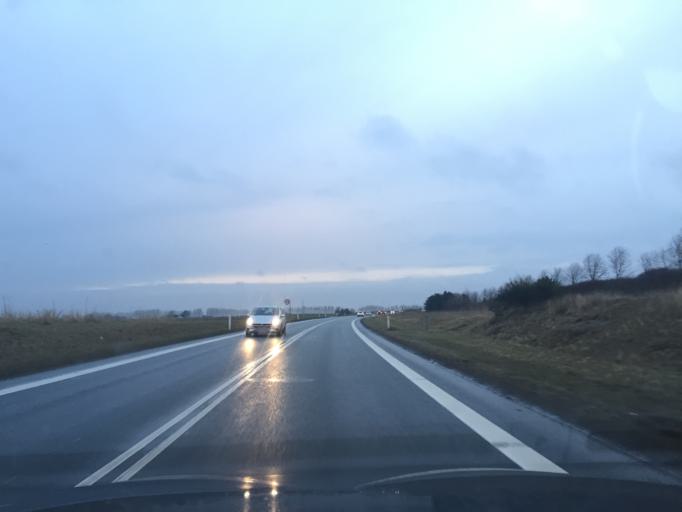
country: DK
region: Zealand
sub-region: Slagelse Kommune
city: Slagelse
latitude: 55.3695
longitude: 11.3283
